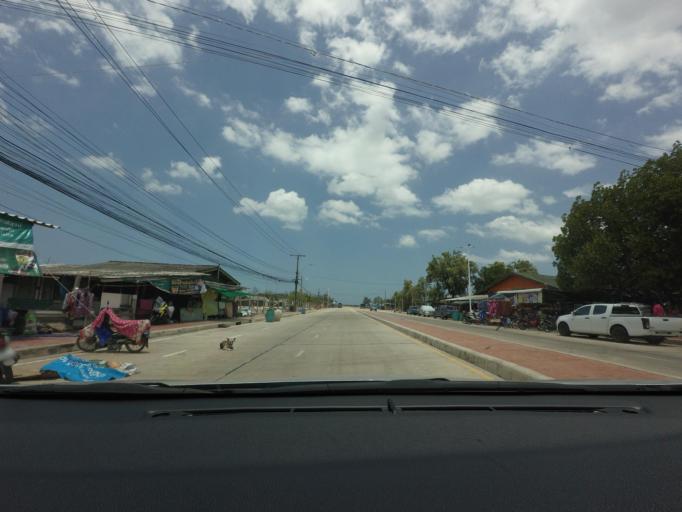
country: TH
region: Samut Prakan
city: Samut Prakan
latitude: 13.5564
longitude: 100.5894
